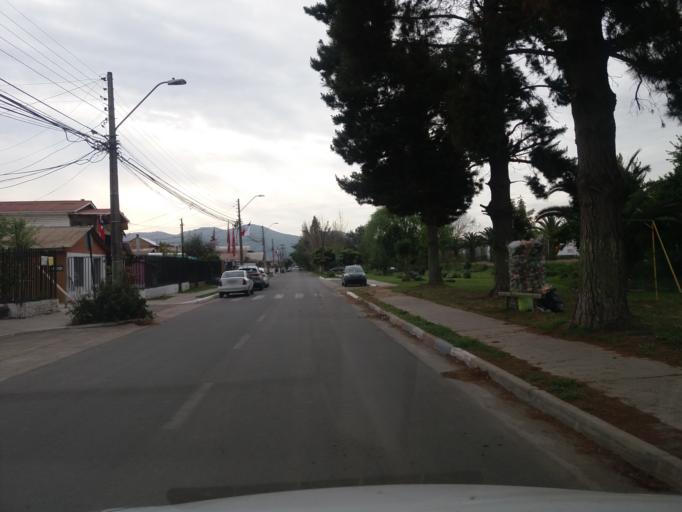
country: CL
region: Valparaiso
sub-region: Provincia de Quillota
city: Hacienda La Calera
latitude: -32.7853
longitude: -71.1723
